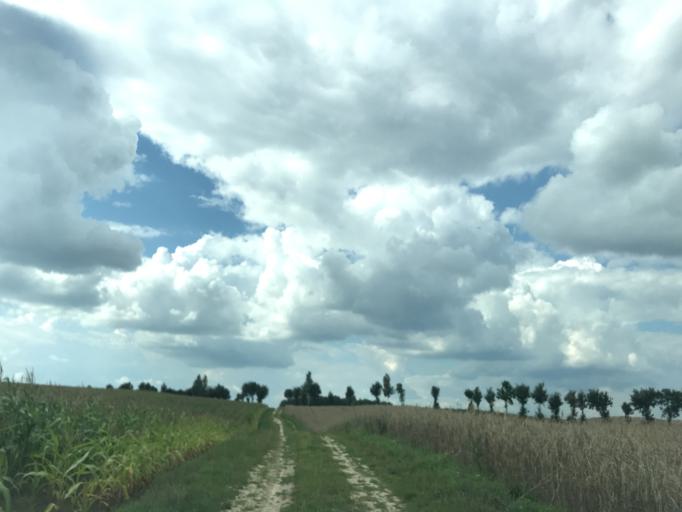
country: PL
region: Kujawsko-Pomorskie
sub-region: Powiat brodnicki
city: Brzozie
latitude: 53.3265
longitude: 19.6784
